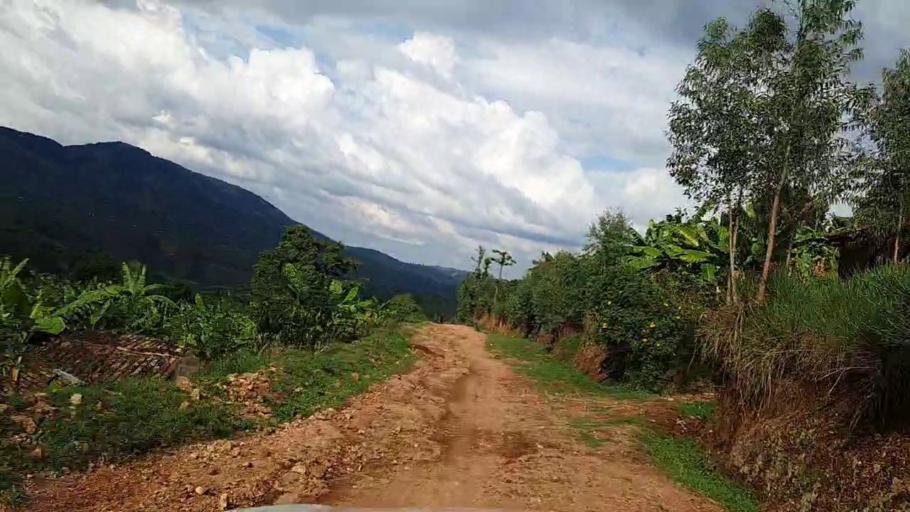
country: RW
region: Southern Province
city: Gikongoro
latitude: -2.4263
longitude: 29.6403
